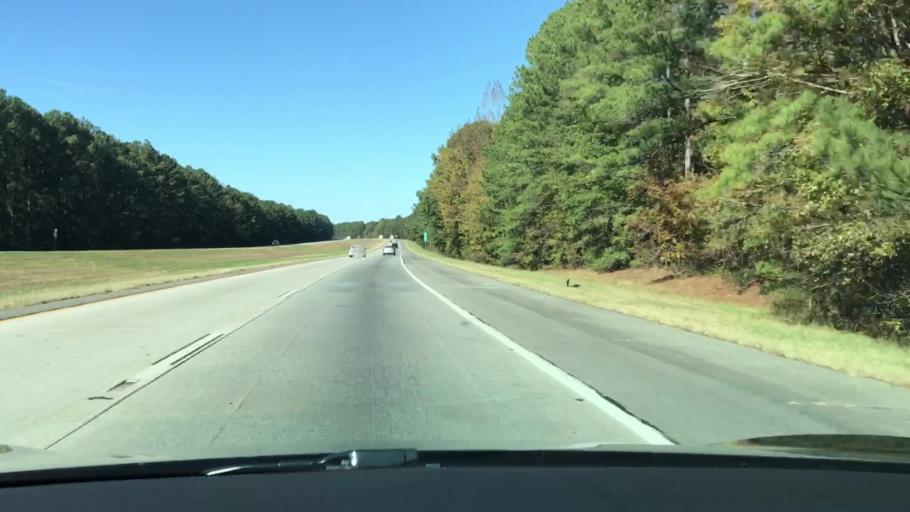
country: US
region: Georgia
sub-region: Taliaferro County
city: Crawfordville
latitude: 33.5334
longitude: -82.9894
